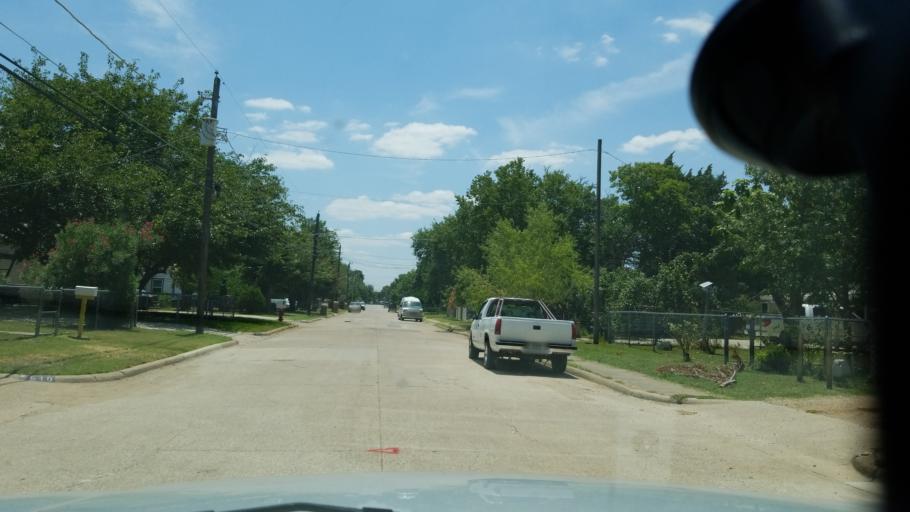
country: US
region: Texas
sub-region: Dallas County
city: Grand Prairie
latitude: 32.7548
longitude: -96.9616
